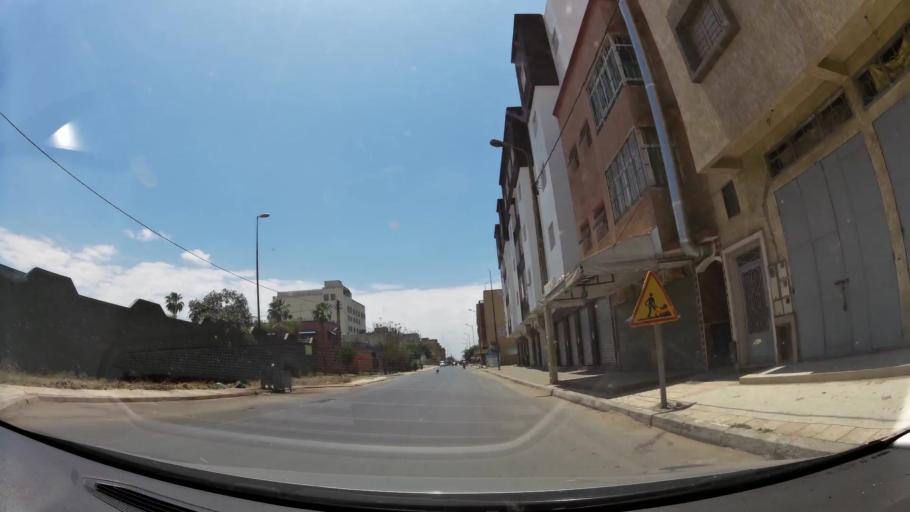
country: MA
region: Gharb-Chrarda-Beni Hssen
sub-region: Kenitra Province
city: Kenitra
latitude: 34.2378
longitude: -6.6173
